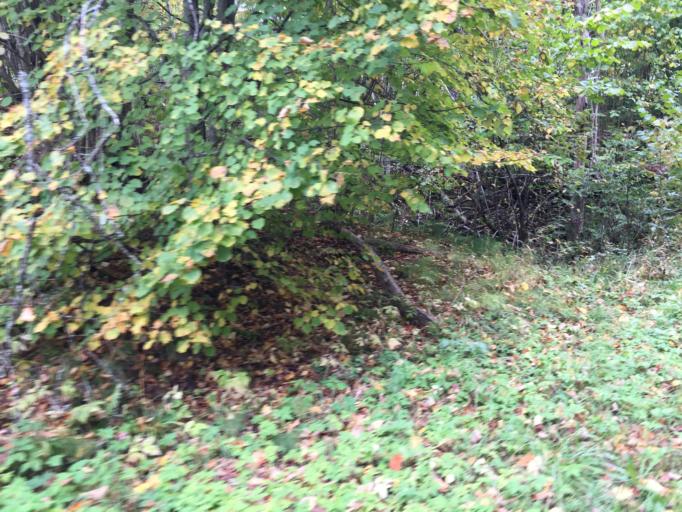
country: LV
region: Ligatne
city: Ligatne
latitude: 57.2135
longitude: 25.0643
